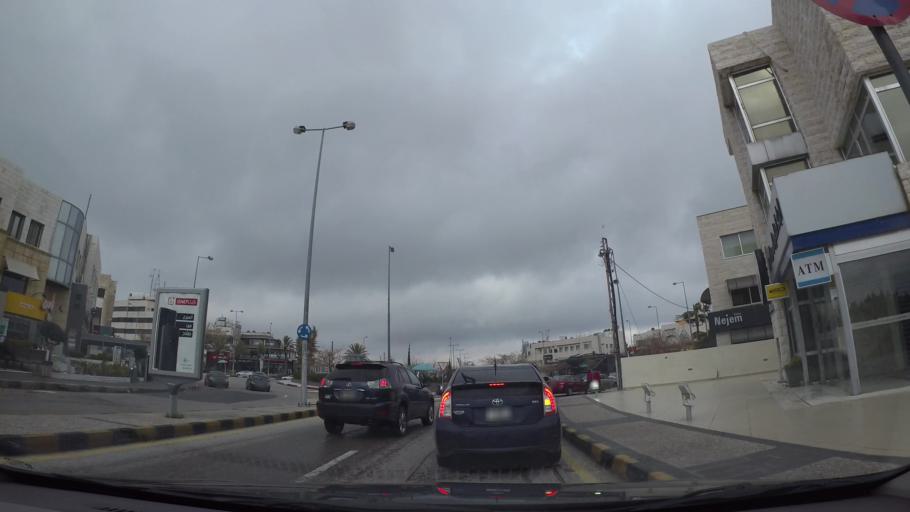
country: JO
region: Amman
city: Amman
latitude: 31.9482
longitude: 35.8924
